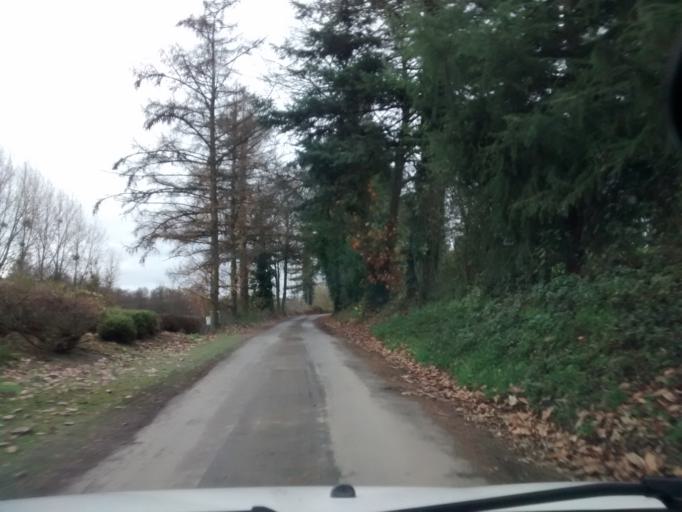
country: FR
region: Brittany
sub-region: Departement d'Ille-et-Vilaine
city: Argentre-du-Plessis
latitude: 48.0805
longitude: -1.1663
